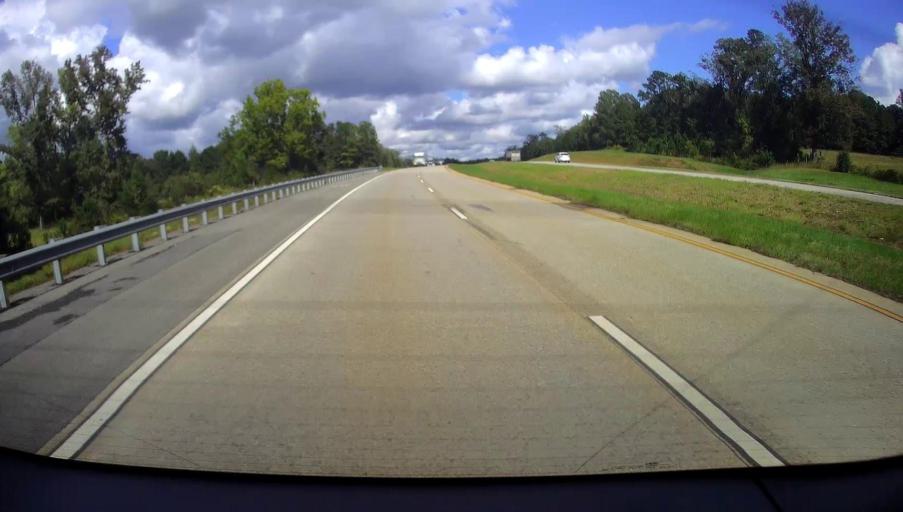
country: US
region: Georgia
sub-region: Jones County
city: Gray
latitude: 33.0107
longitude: -83.5727
